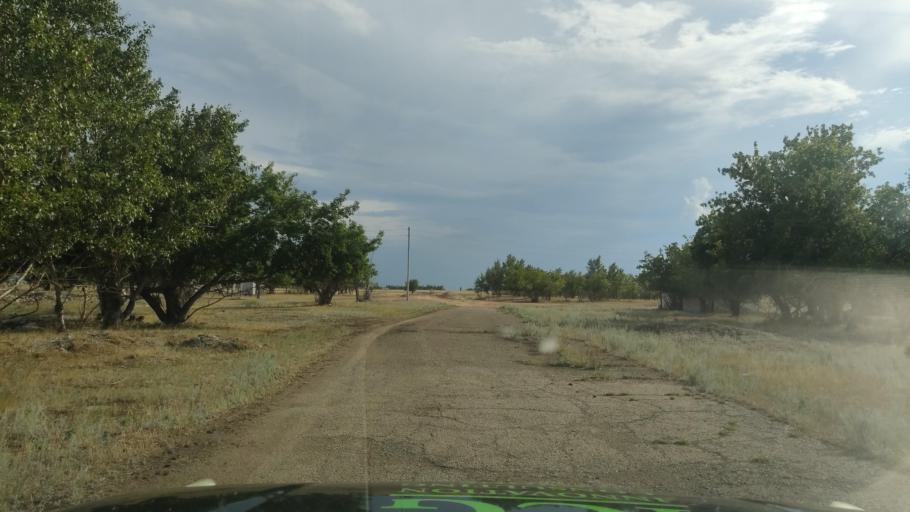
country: KZ
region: Pavlodar
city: Pavlodar
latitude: 52.5165
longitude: 77.4416
